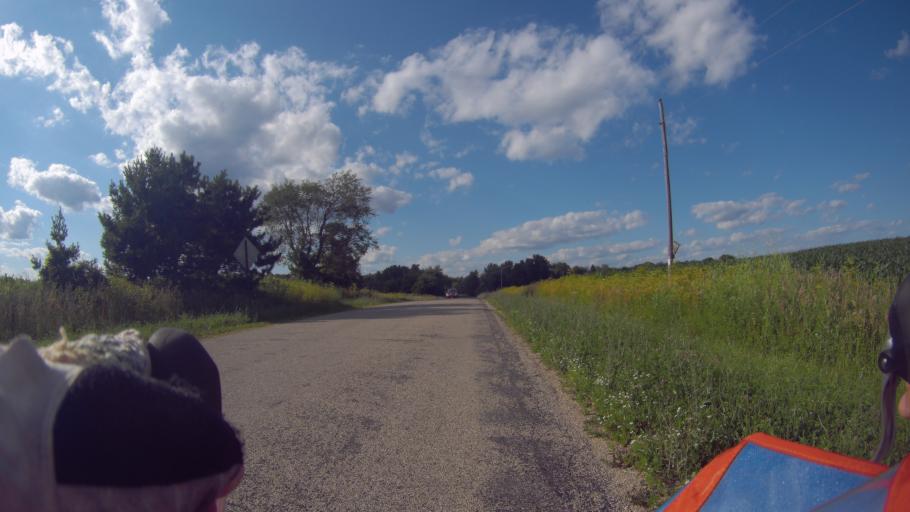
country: US
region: Wisconsin
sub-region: Dane County
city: McFarland
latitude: 42.9354
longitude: -89.2939
